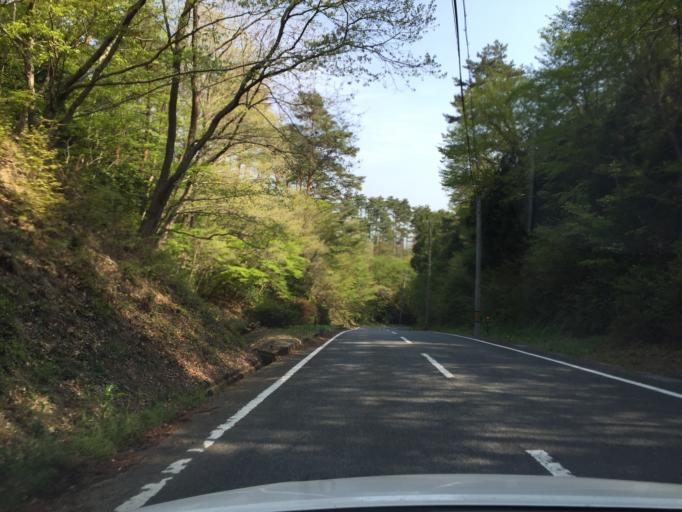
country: JP
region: Fukushima
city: Iwaki
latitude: 37.1619
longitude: 140.8538
